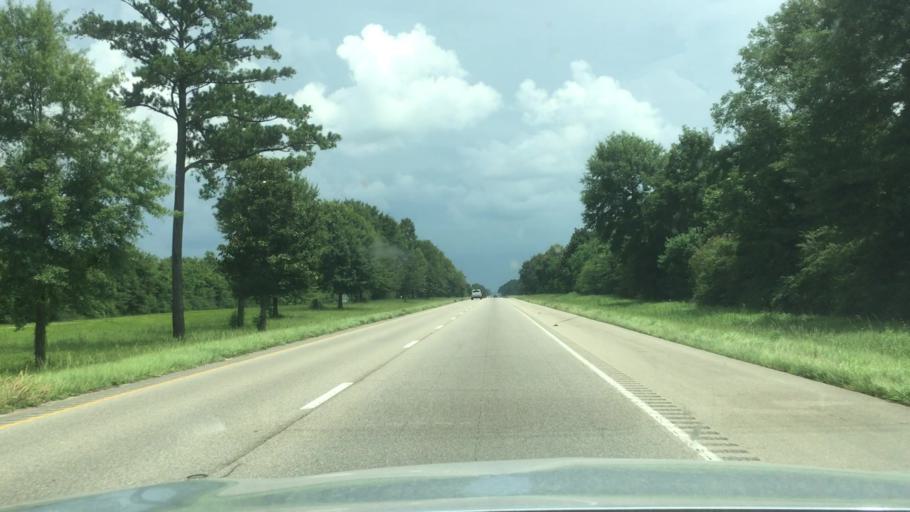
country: US
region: Mississippi
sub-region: Pearl River County
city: Picayune
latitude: 30.5564
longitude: -89.6422
